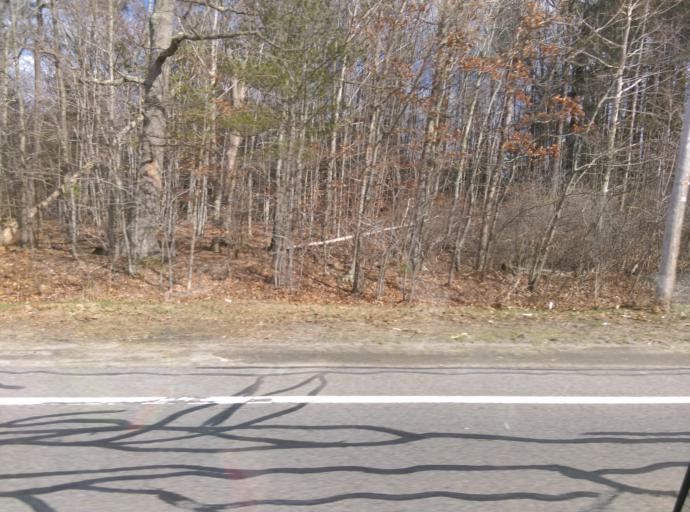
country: US
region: Massachusetts
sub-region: Essex County
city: Salisbury
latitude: 42.8621
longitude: -70.8898
